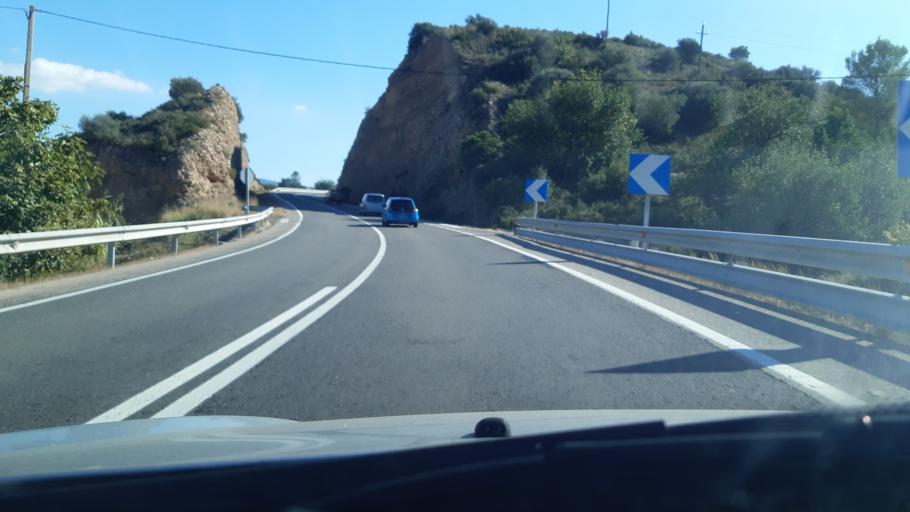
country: ES
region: Catalonia
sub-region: Provincia de Tarragona
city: Tivenys
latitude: 40.8826
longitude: 0.4950
